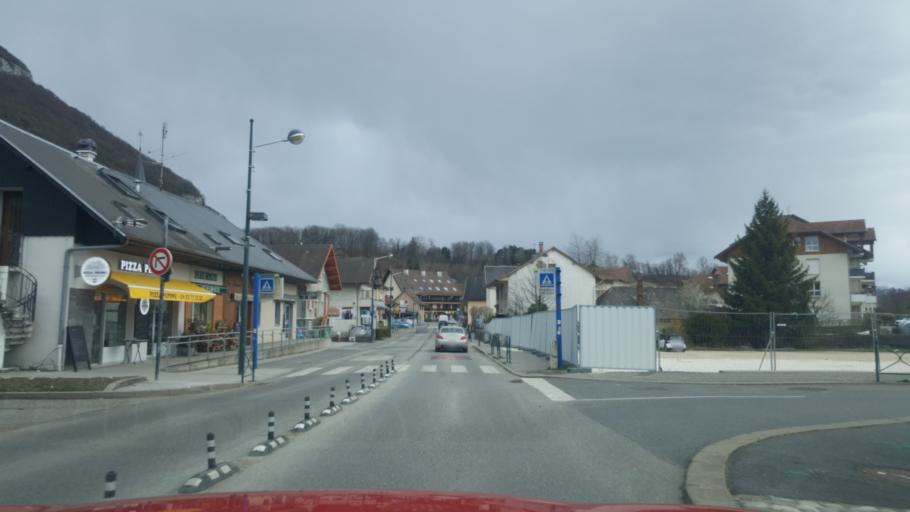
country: FR
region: Rhone-Alpes
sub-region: Departement de la Haute-Savoie
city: La Balme-de-Sillingy
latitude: 45.9617
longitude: 6.0398
